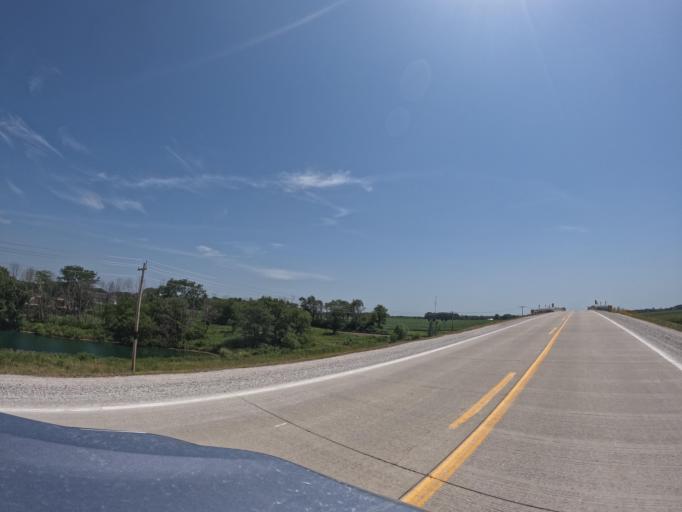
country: US
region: Iowa
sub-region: Henry County
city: Mount Pleasant
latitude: 40.9773
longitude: -91.6126
